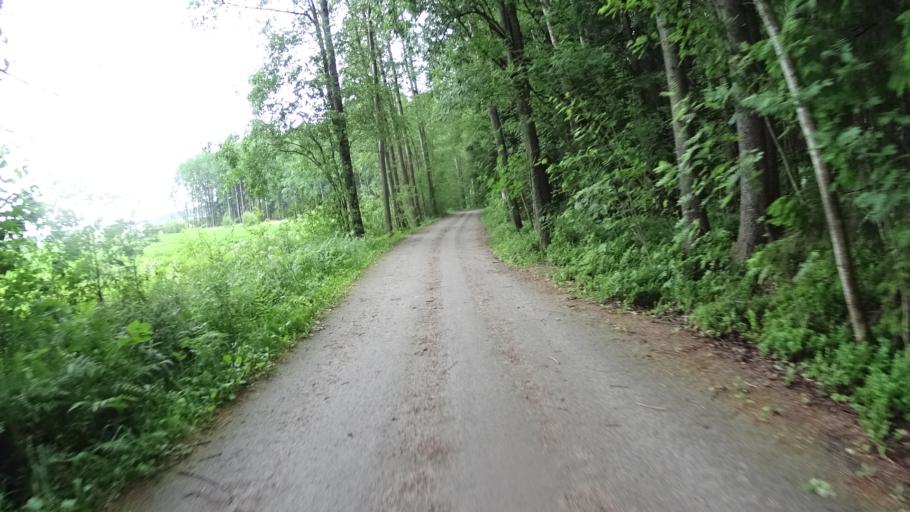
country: FI
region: Uusimaa
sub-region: Helsinki
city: Helsinki
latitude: 60.2690
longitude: 24.9342
